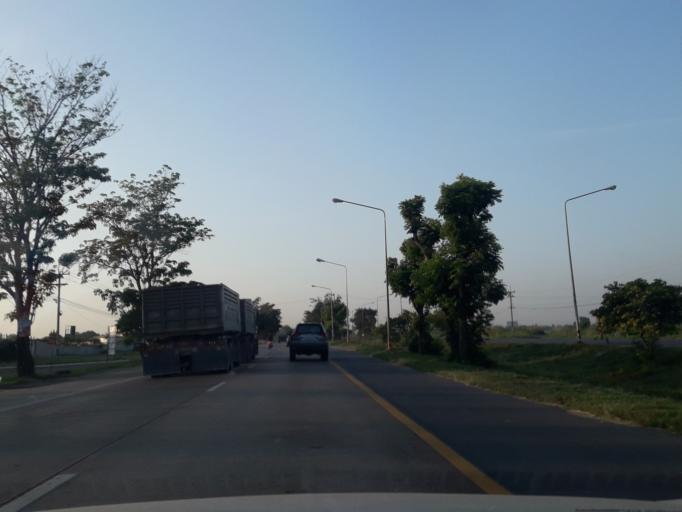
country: TH
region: Phra Nakhon Si Ayutthaya
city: Phra Nakhon Si Ayutthaya
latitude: 14.3370
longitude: 100.5281
